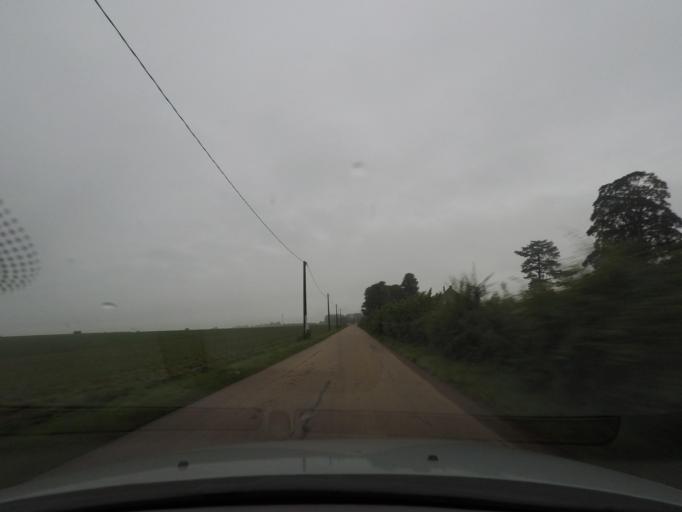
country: FR
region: Haute-Normandie
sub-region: Departement de la Seine-Maritime
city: Saint-Martin-Osmonville
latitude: 49.5967
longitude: 1.2414
